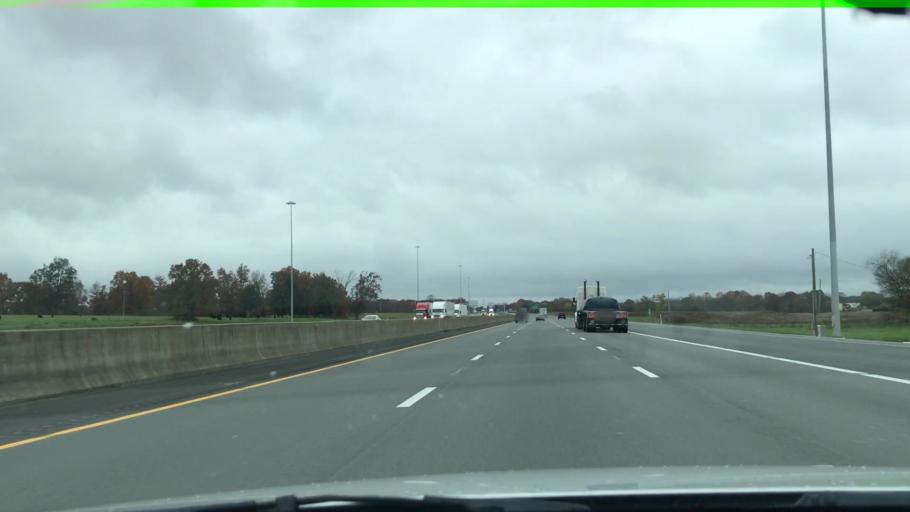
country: US
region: Kentucky
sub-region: Warren County
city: Bowling Green
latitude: 37.0116
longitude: -86.3324
